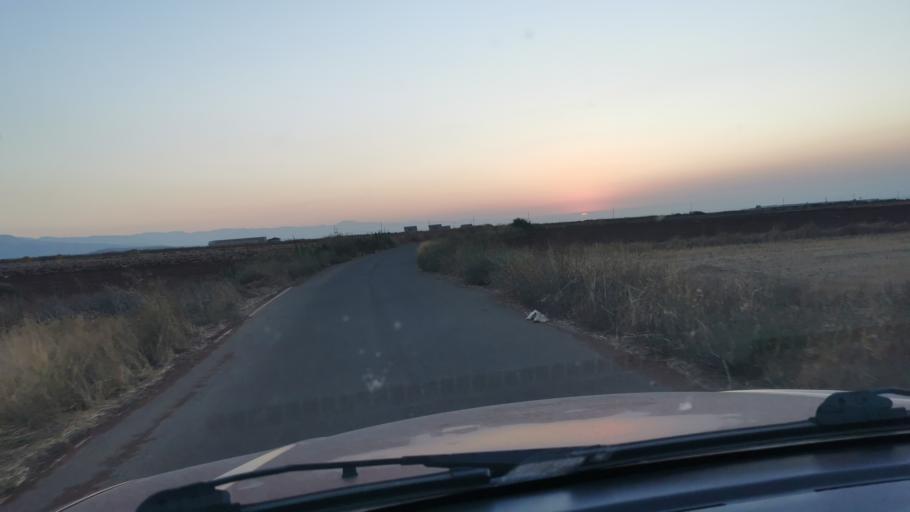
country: CY
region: Lefkosia
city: Peristerona
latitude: 35.0984
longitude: 33.0813
